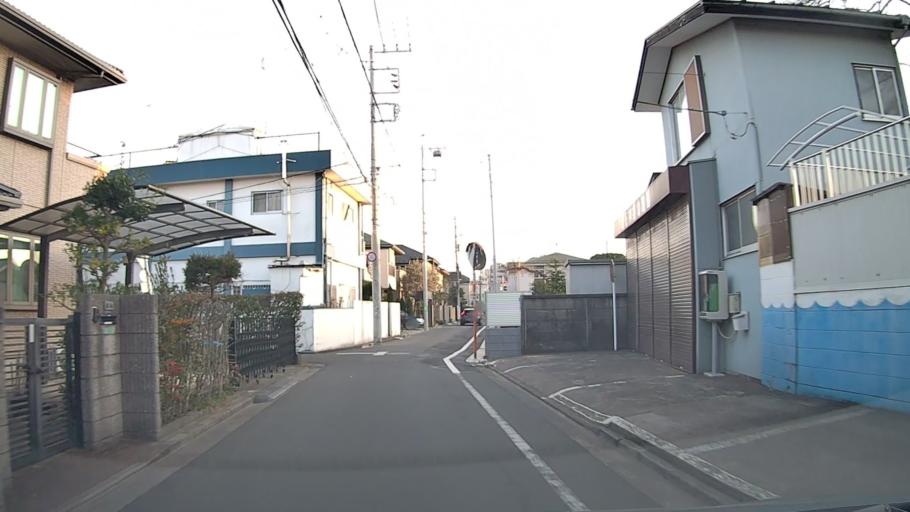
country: JP
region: Tokyo
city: Musashino
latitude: 35.7352
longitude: 139.5797
